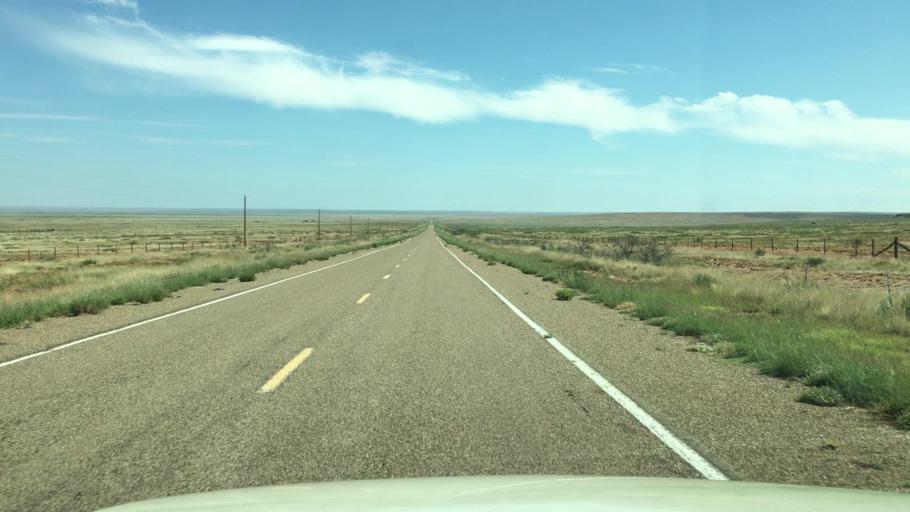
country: US
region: New Mexico
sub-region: De Baca County
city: Fort Sumner
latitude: 33.9827
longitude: -104.5740
